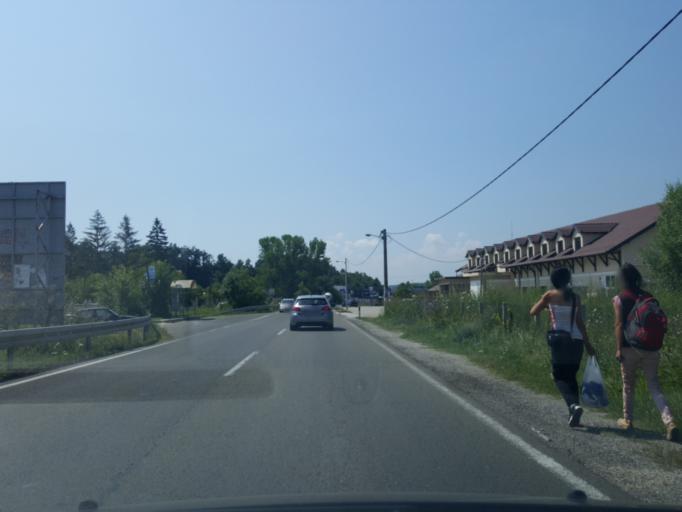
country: RS
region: Central Serbia
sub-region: Belgrade
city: Mladenovac
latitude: 44.4914
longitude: 20.6574
